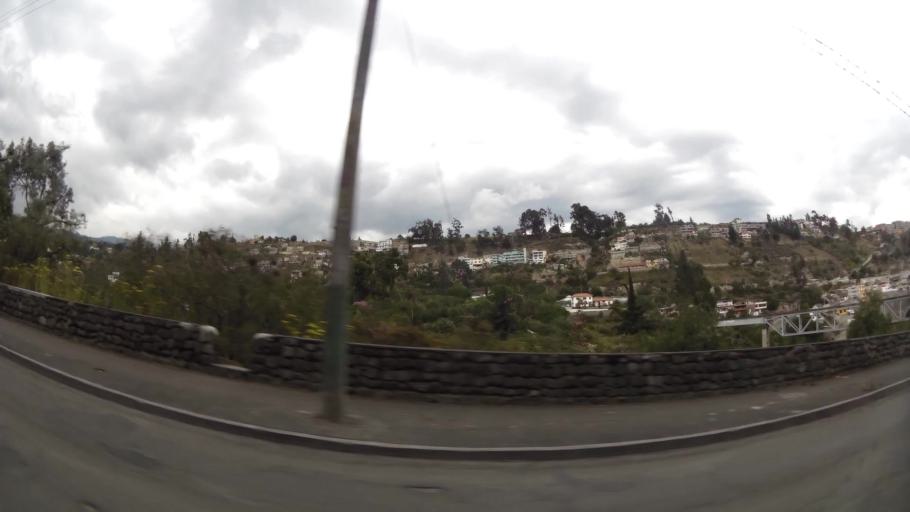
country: EC
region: Tungurahua
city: Ambato
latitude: -1.2291
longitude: -78.6209
